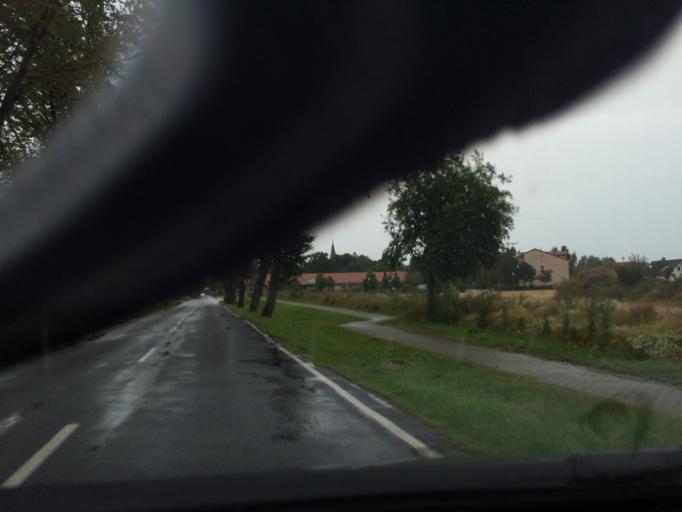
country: DE
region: Mecklenburg-Vorpommern
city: Prohn
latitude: 54.3648
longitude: 13.0280
